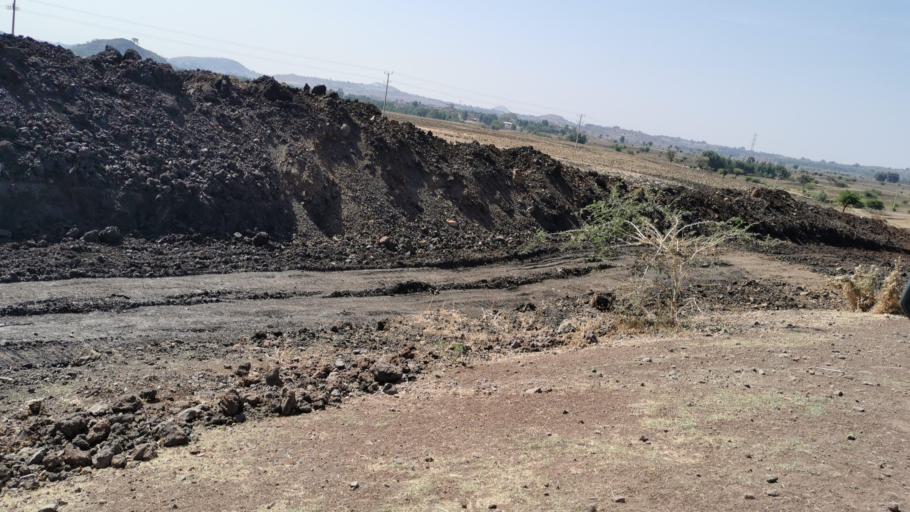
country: ET
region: Amhara
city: Bahir Dar
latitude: 11.8385
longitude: 37.0015
